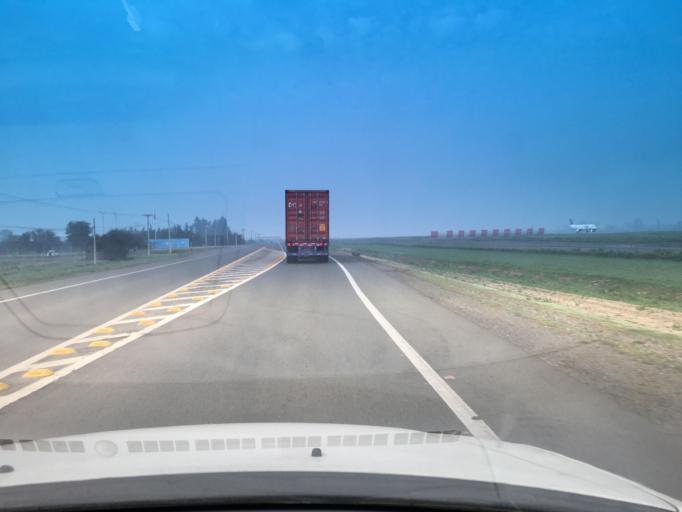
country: CL
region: Santiago Metropolitan
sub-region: Provincia de Santiago
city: Lo Prado
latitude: -33.3771
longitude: -70.7991
